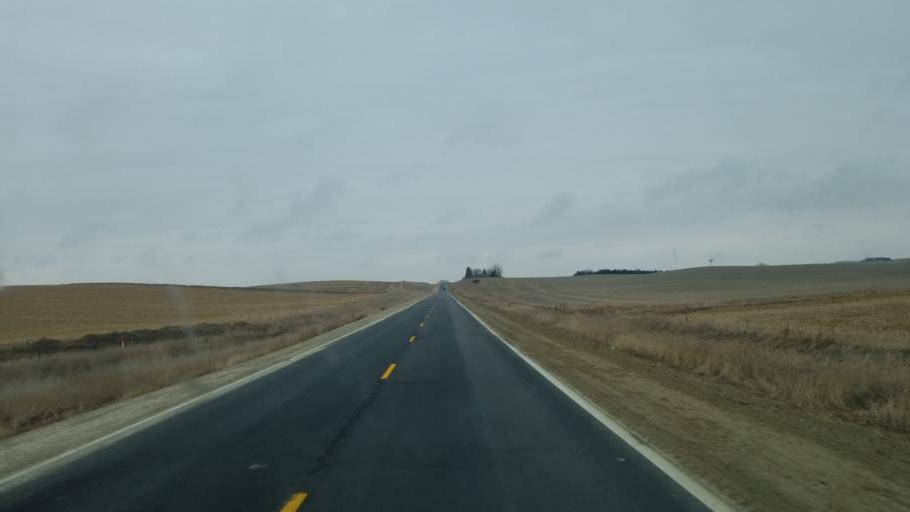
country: US
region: Nebraska
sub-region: Knox County
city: Bloomfield
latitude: 42.5977
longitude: -97.6760
